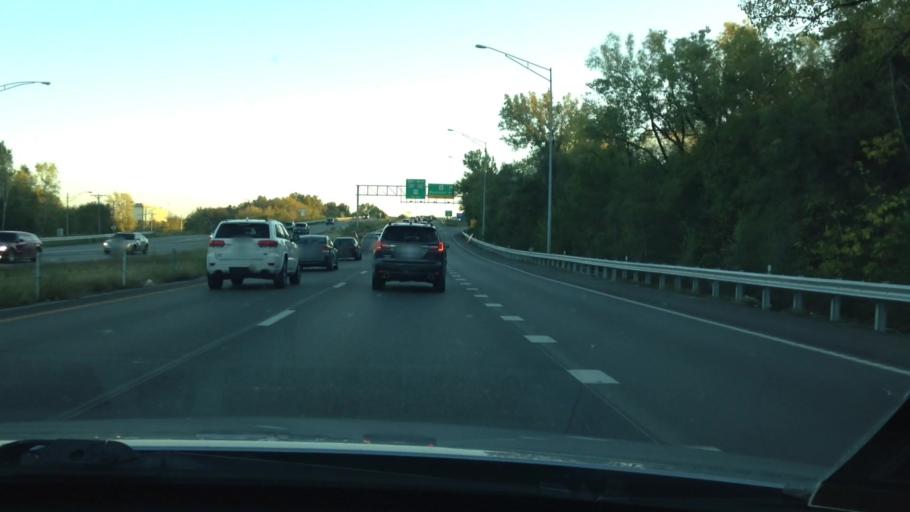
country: US
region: Missouri
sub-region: Jackson County
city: Grandview
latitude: 38.9572
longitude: -94.5411
